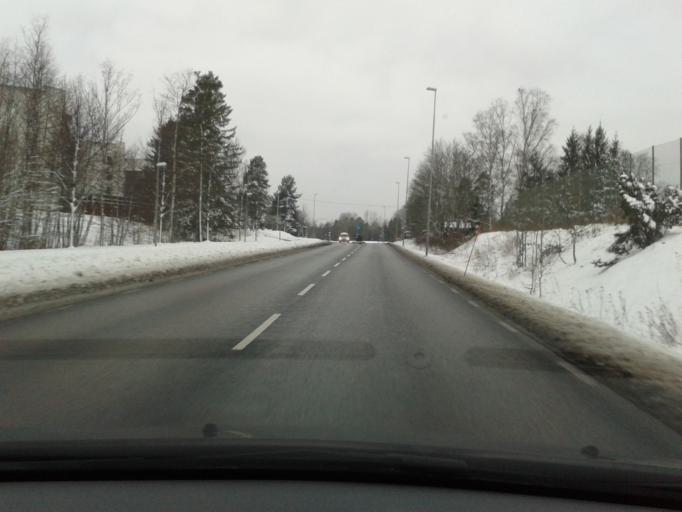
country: SE
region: Stockholm
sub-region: Tyreso Kommun
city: Bollmora
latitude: 59.2493
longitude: 18.2389
